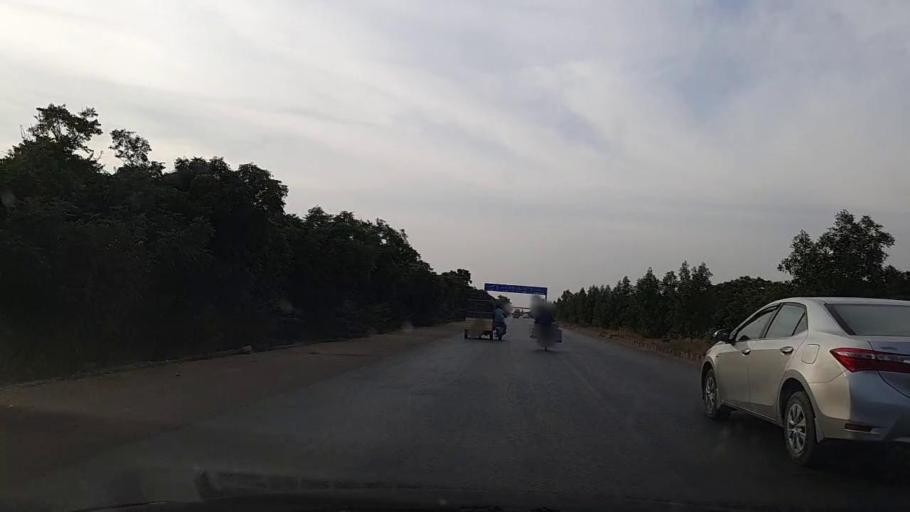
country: PK
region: Sindh
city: Gharo
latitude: 24.8519
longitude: 67.4202
